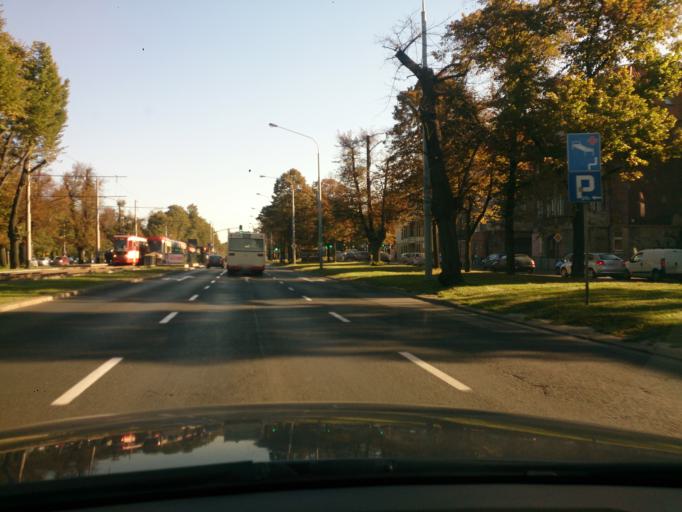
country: PL
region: Pomeranian Voivodeship
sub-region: Gdansk
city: Gdansk
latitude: 54.3697
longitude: 18.6286
